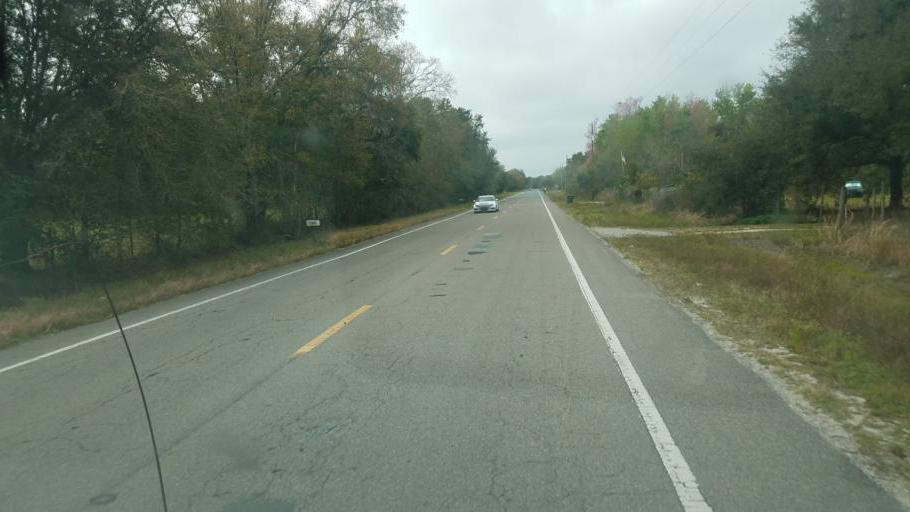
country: US
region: Florida
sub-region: Polk County
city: Gibsonia
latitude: 28.2265
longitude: -81.9800
